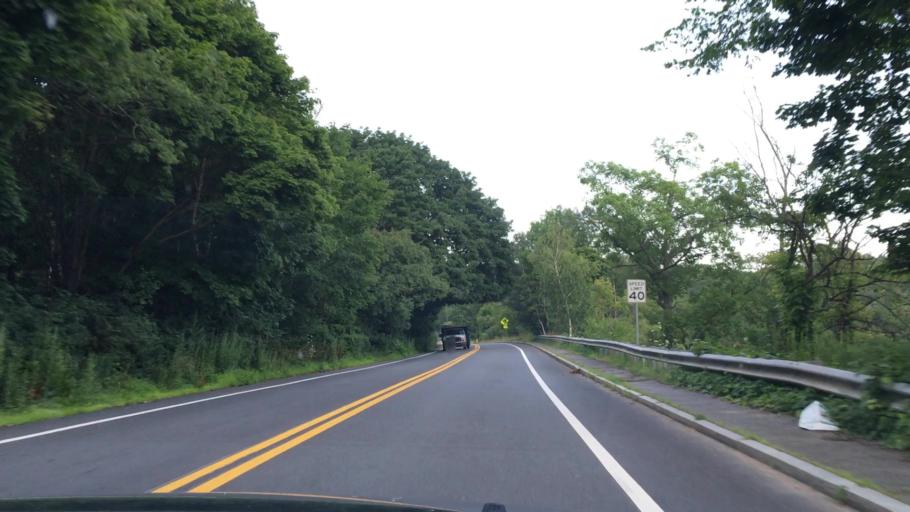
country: US
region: Massachusetts
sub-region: Essex County
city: Essex
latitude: 42.5798
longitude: -70.7567
